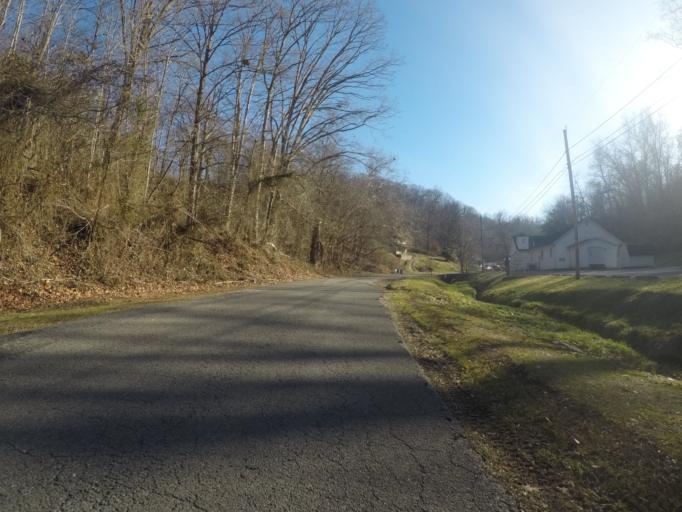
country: US
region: West Virginia
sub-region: Cabell County
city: Huntington
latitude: 38.3936
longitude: -82.4861
